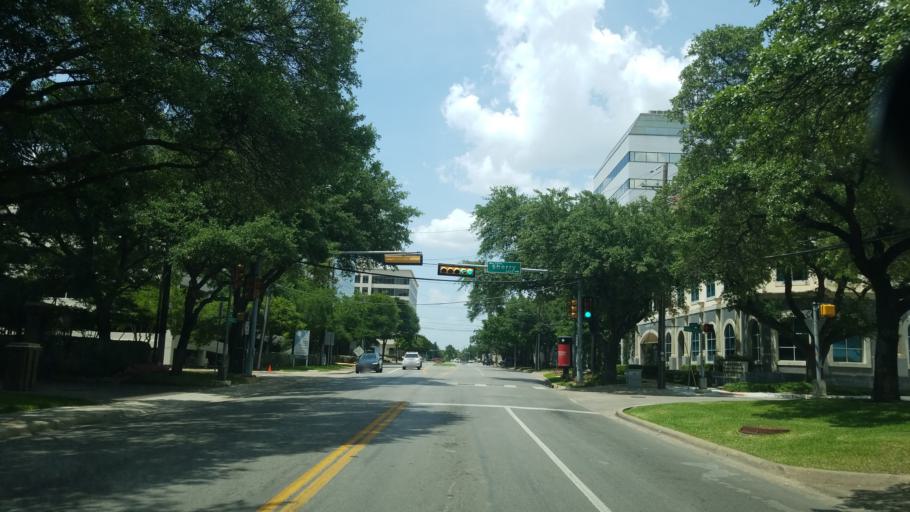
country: US
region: Texas
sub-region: Dallas County
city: University Park
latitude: 32.8619
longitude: -96.8086
